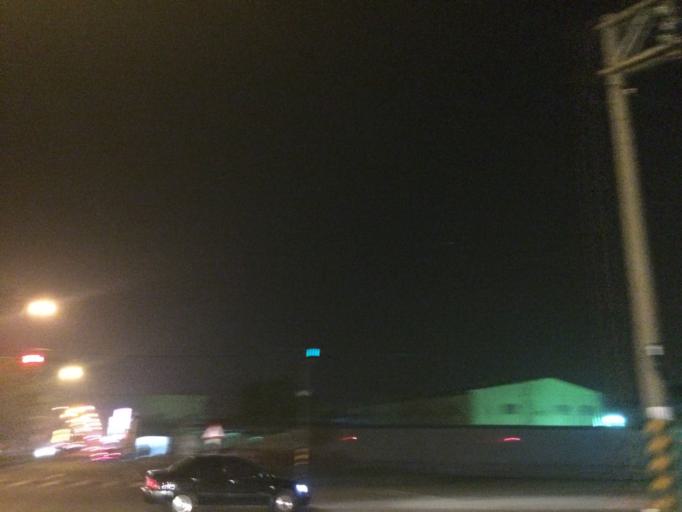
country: TW
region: Taiwan
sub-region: Miaoli
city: Miaoli
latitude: 24.6749
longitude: 120.8836
